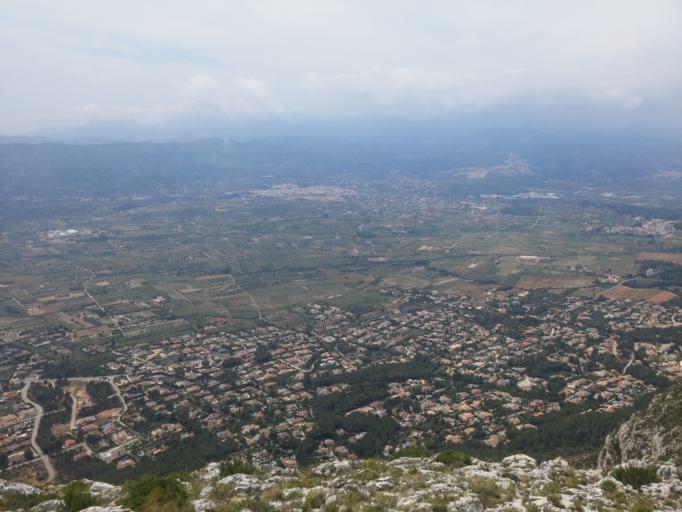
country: ES
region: Valencia
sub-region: Provincia de Alicante
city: Denia
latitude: 38.8048
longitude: 0.1271
